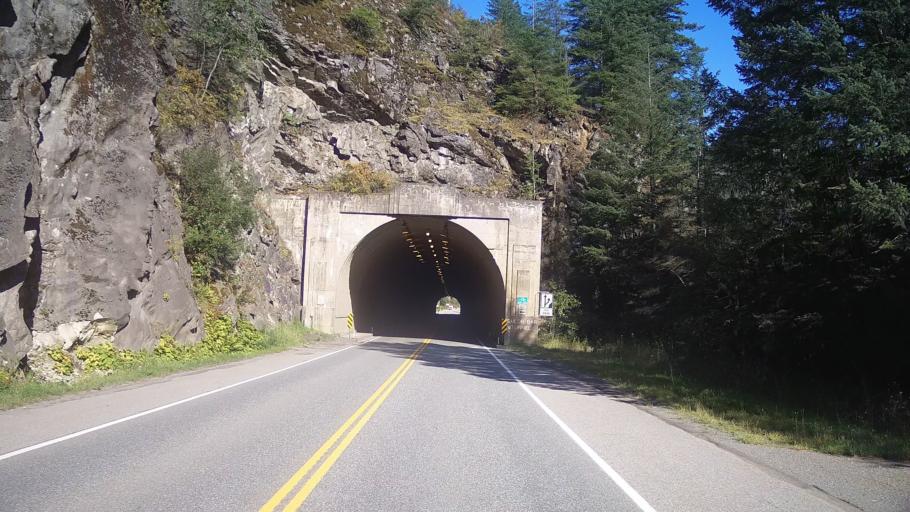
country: CA
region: British Columbia
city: Hope
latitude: 49.6364
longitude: -121.4017
